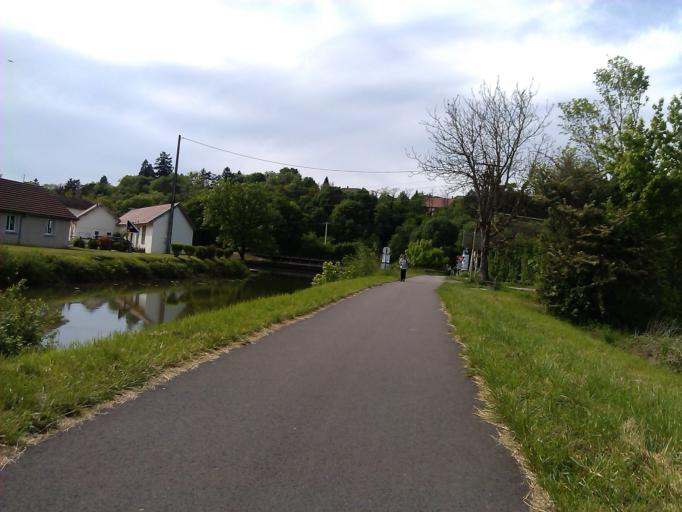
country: FR
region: Franche-Comte
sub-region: Departement du Doubs
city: Saint-Vit
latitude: 47.1743
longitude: 5.7948
